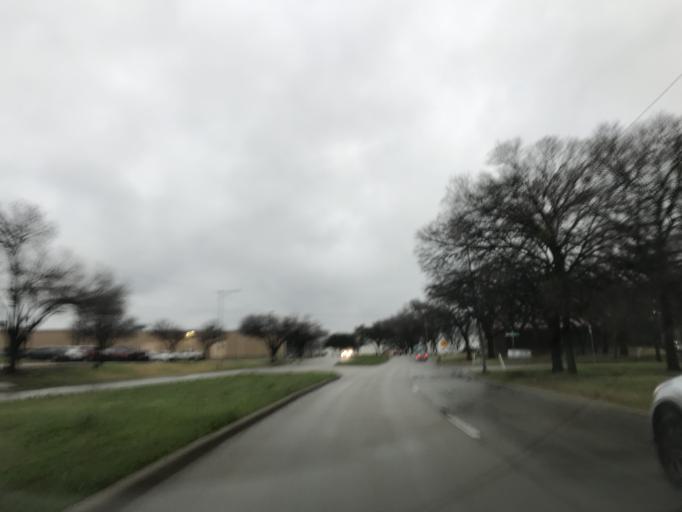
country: US
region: Texas
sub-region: Dallas County
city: Grand Prairie
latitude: 32.7730
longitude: -97.0557
